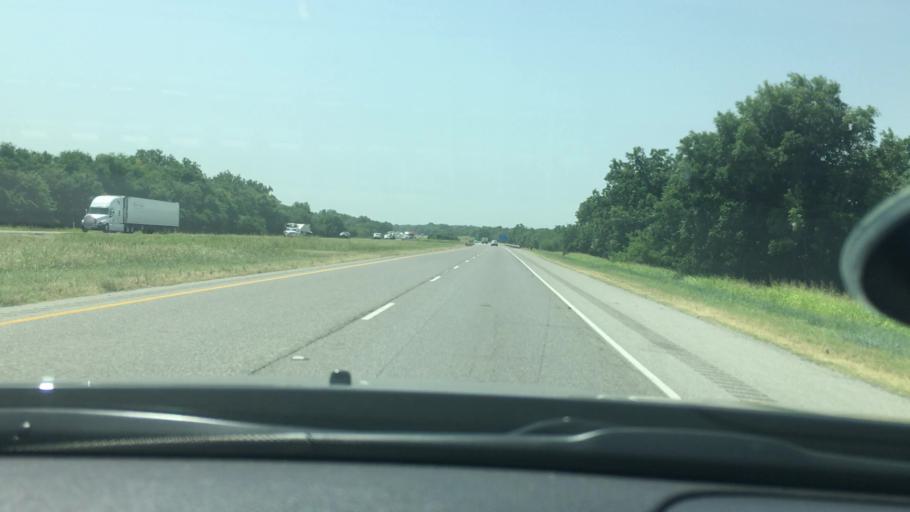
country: US
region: Oklahoma
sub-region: Murray County
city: Davis
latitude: 34.5295
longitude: -97.1866
